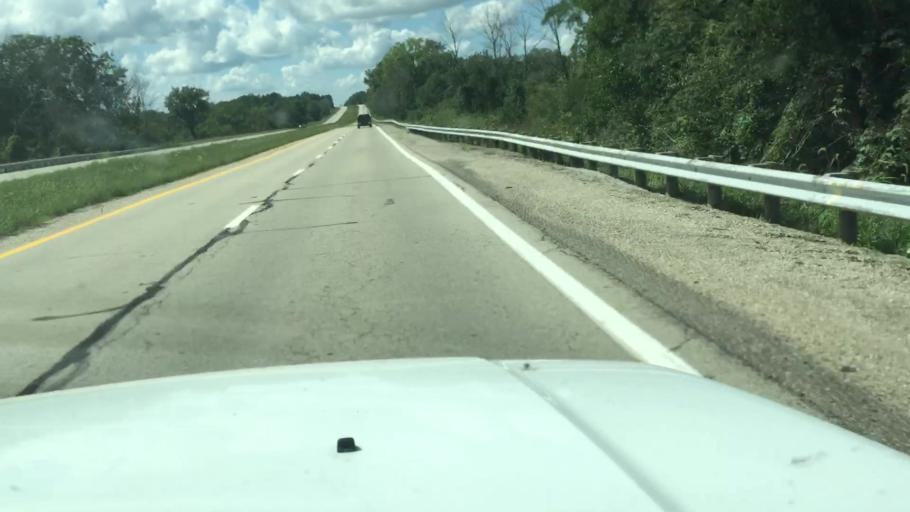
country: US
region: Ohio
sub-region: Madison County
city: Choctaw Lake
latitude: 39.9325
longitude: -83.5202
